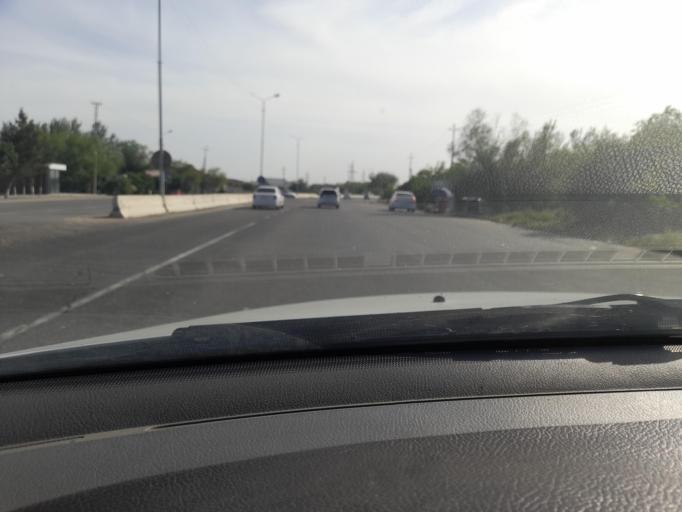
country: UZ
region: Samarqand
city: Kattaqo'rg'on
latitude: 39.9247
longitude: 66.2391
